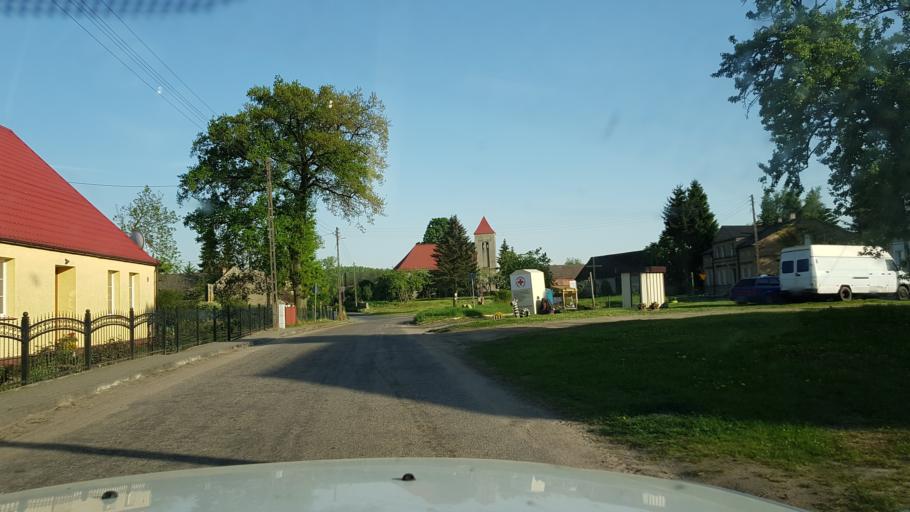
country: PL
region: West Pomeranian Voivodeship
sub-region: Powiat lobeski
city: Dobra
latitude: 53.6331
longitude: 15.3599
